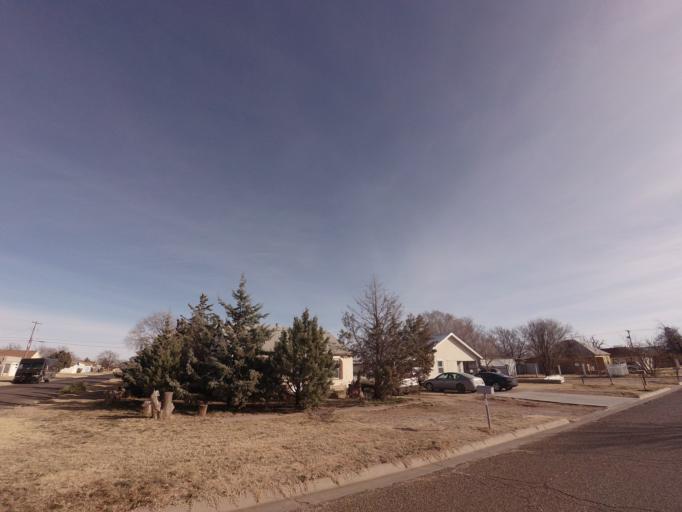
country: US
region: New Mexico
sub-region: Curry County
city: Clovis
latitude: 34.4077
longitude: -103.2155
